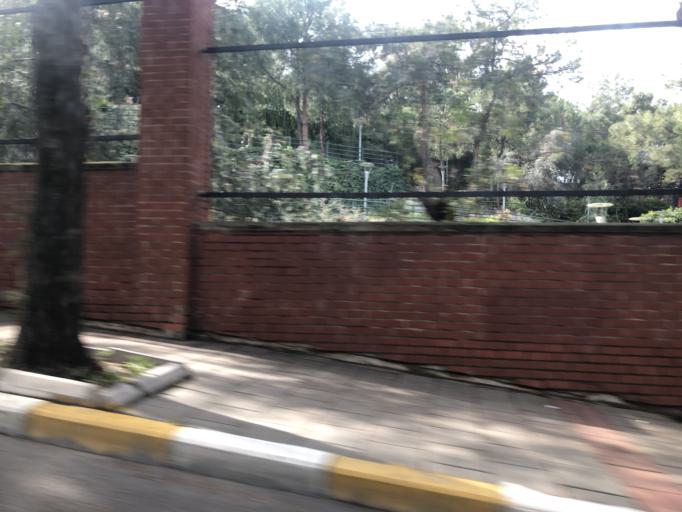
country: TR
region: Izmir
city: Karabaglar
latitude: 38.3890
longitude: 27.0458
